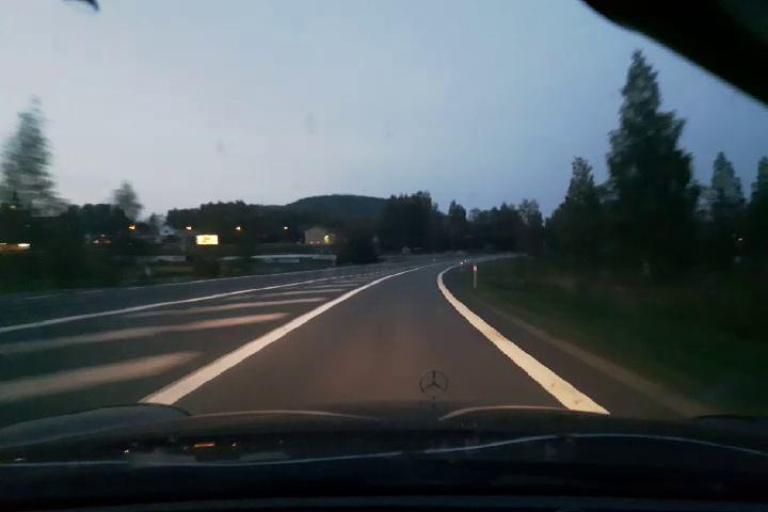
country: SE
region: Vaesternorrland
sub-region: Kramfors Kommun
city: Nordingra
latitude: 63.0558
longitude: 18.3332
